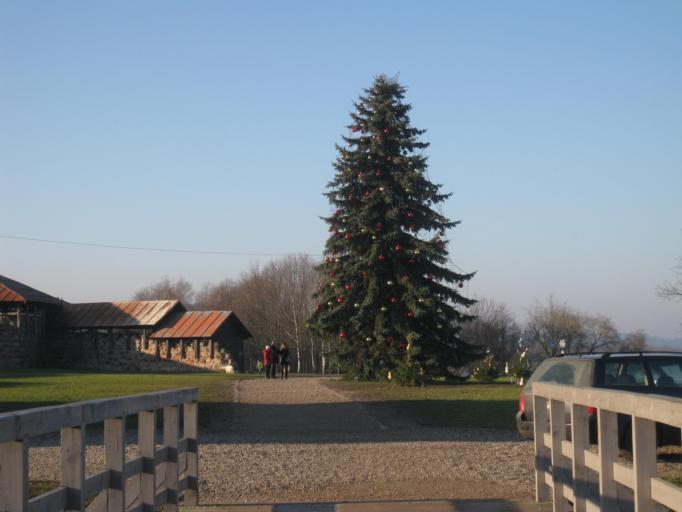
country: LT
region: Kauno apskritis
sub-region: Kaunas
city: Kaunas
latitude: 54.8993
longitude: 23.8860
